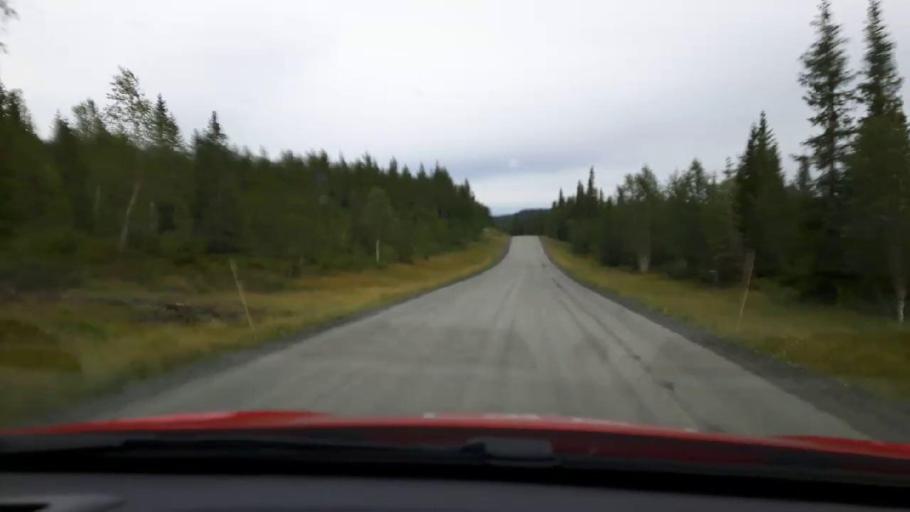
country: SE
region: Jaemtland
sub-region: Are Kommun
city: Are
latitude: 63.4360
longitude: 13.2661
